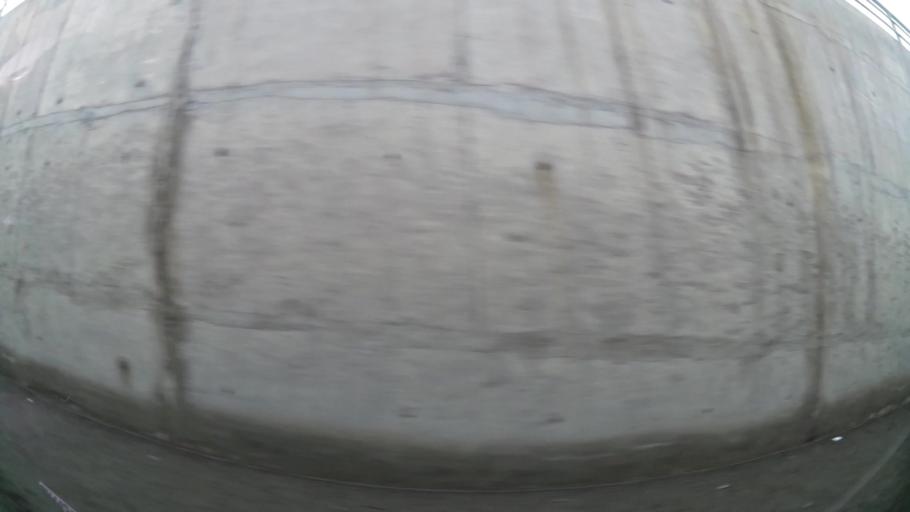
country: XK
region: Pristina
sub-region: Komuna e Prishtines
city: Pristina
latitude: 42.6451
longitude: 21.1561
